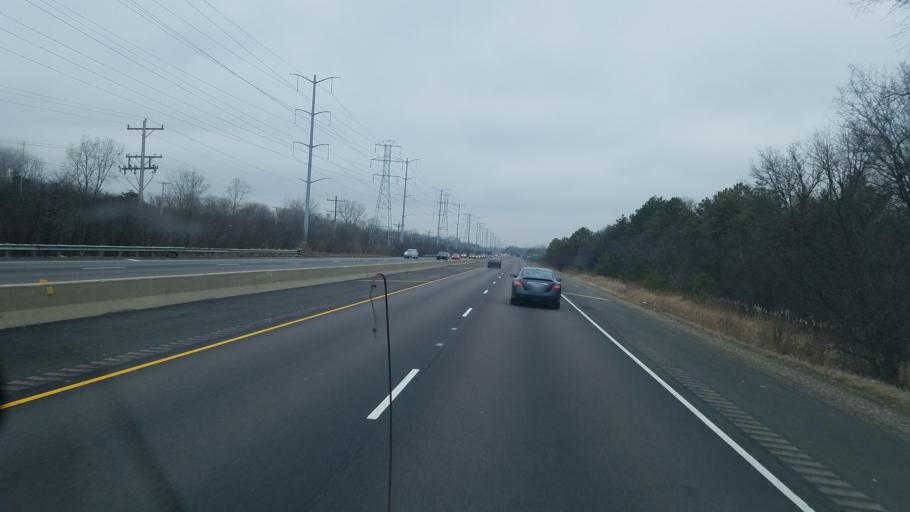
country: US
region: Illinois
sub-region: Lake County
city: Lake Forest
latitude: 42.2248
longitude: -87.8495
